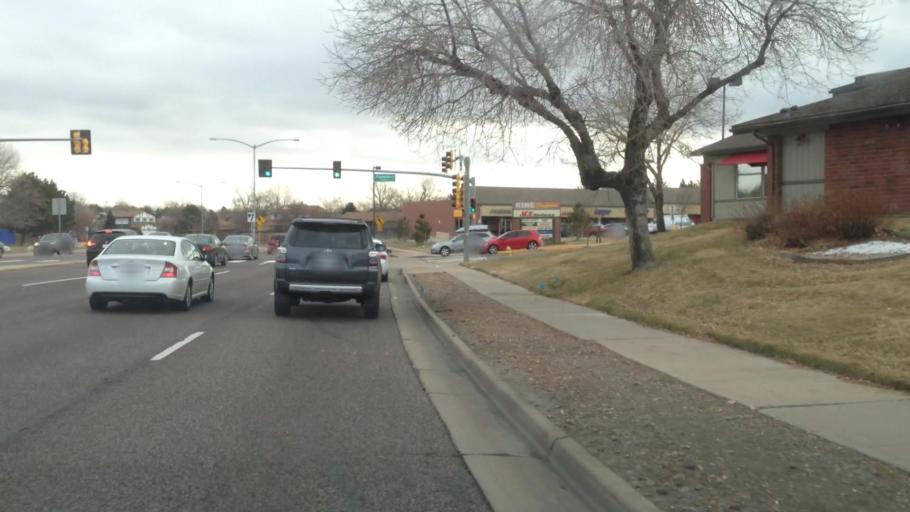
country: US
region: Colorado
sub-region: Adams County
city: Aurora
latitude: 39.6734
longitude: -104.7898
